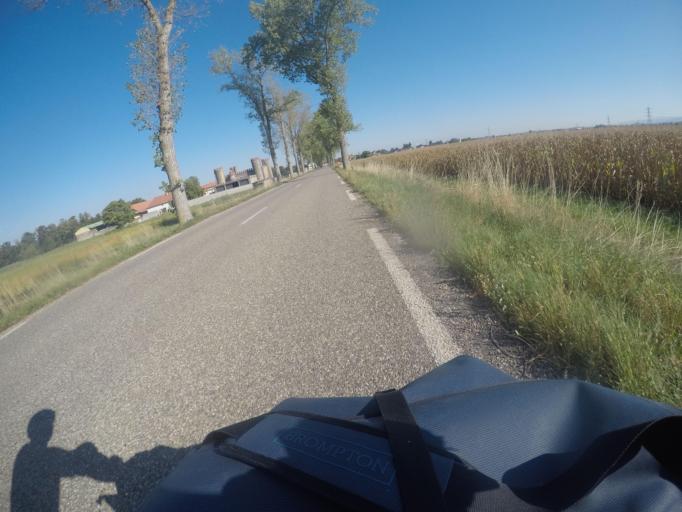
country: FR
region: Alsace
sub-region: Departement du Haut-Rhin
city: Ottmarsheim
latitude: 47.7511
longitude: 7.5049
